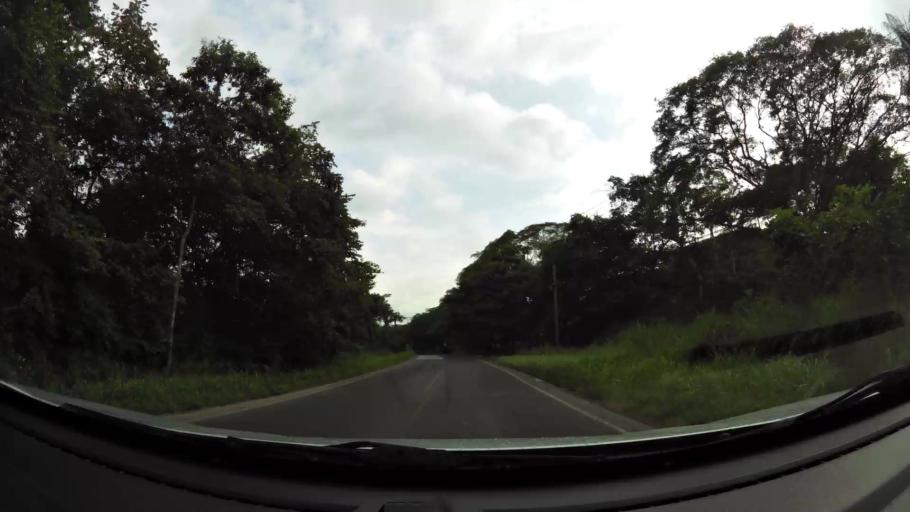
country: CR
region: Guanacaste
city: Juntas
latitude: 10.2007
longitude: -84.9580
